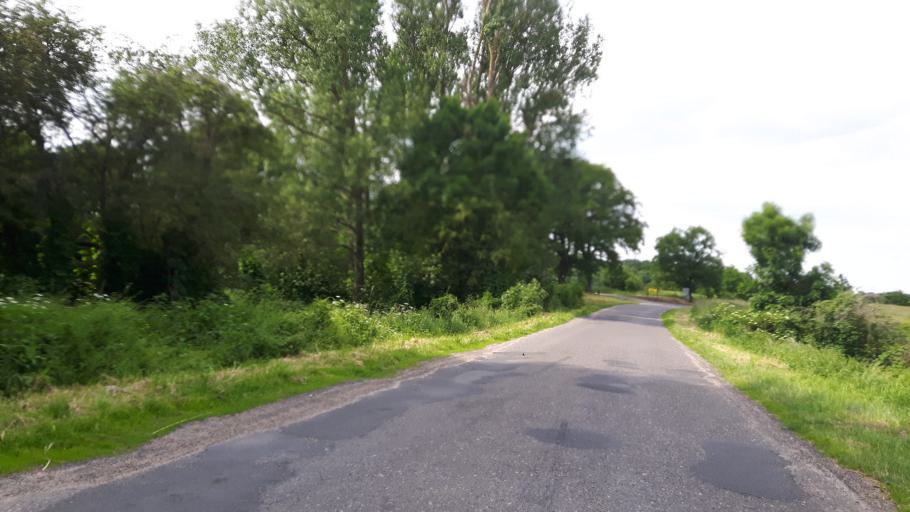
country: PL
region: West Pomeranian Voivodeship
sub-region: Powiat goleniowski
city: Nowogard
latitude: 53.7627
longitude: 15.1154
